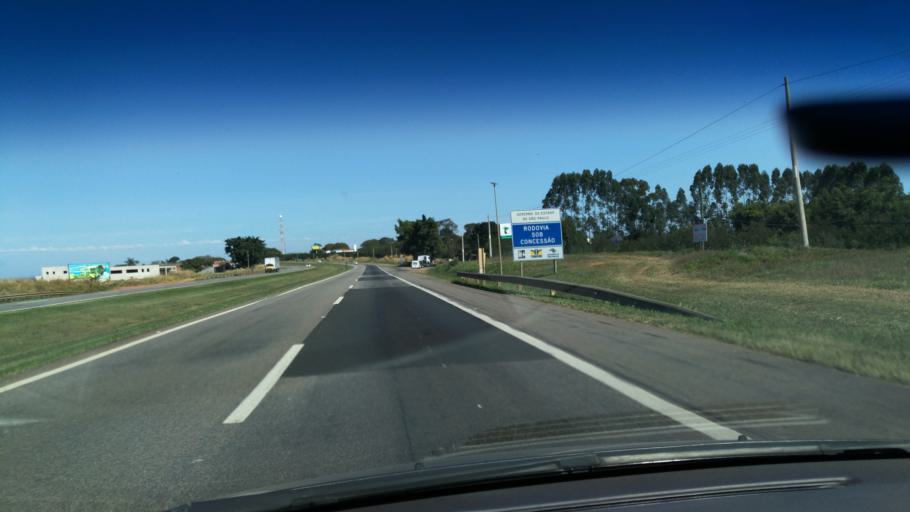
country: BR
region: Sao Paulo
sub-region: Mogi-Mirim
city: Mogi Mirim
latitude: -22.5109
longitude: -46.9891
